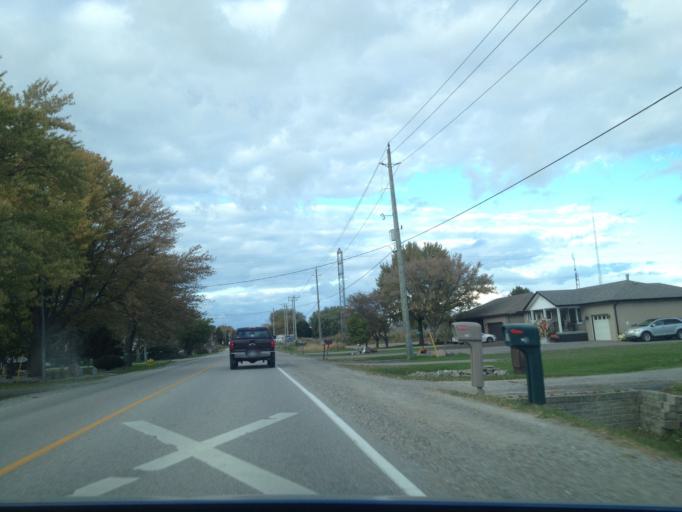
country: US
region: Michigan
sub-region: Wayne County
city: Grosse Pointe Farms
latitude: 42.2823
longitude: -82.7125
